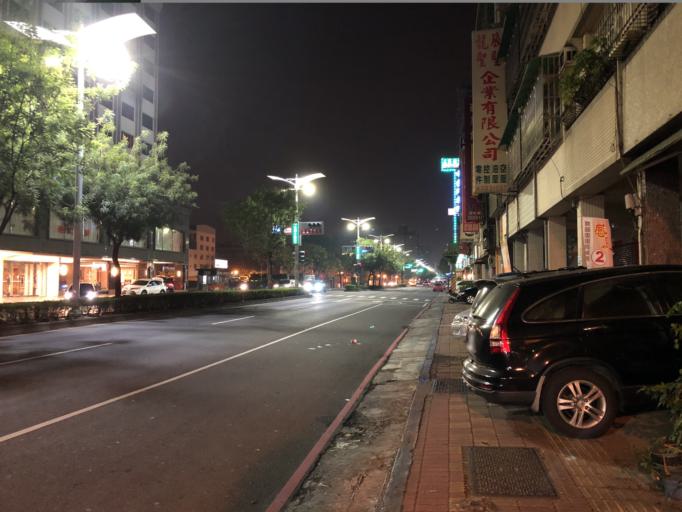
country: TW
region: Kaohsiung
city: Kaohsiung
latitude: 22.6387
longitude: 120.3303
